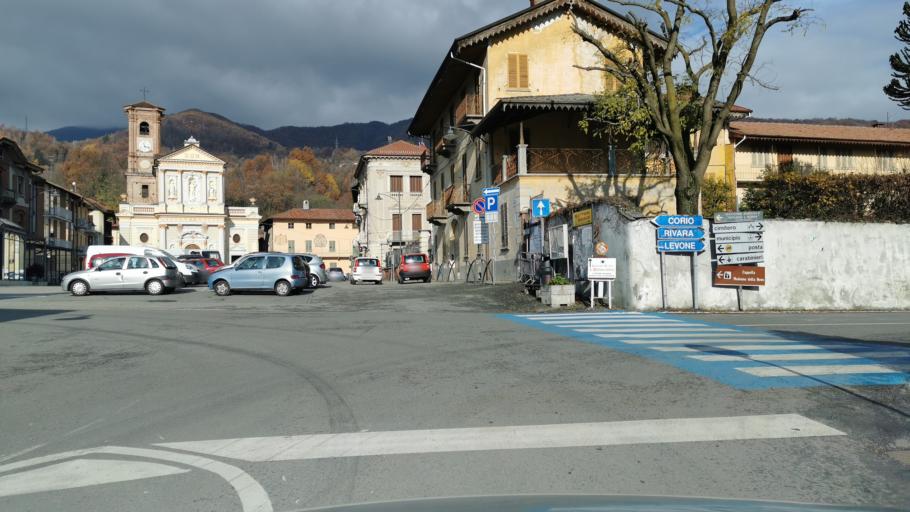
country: IT
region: Piedmont
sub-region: Provincia di Torino
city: Rocca Canavese
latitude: 45.3084
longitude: 7.5763
